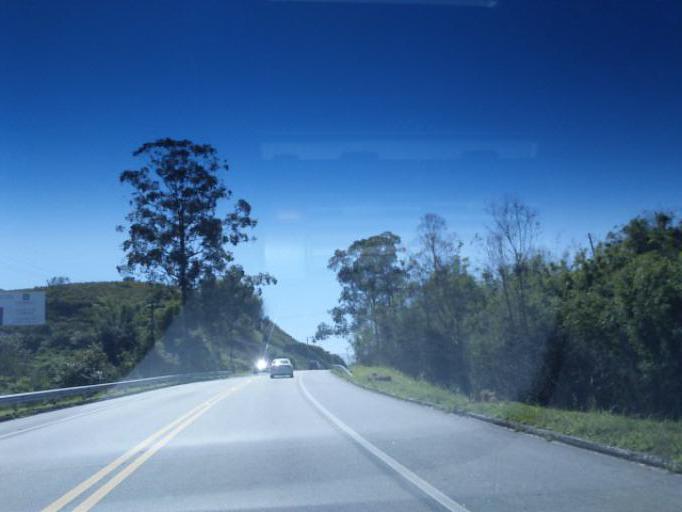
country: BR
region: Sao Paulo
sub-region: Tremembe
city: Tremembe
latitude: -22.9159
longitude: -45.5916
